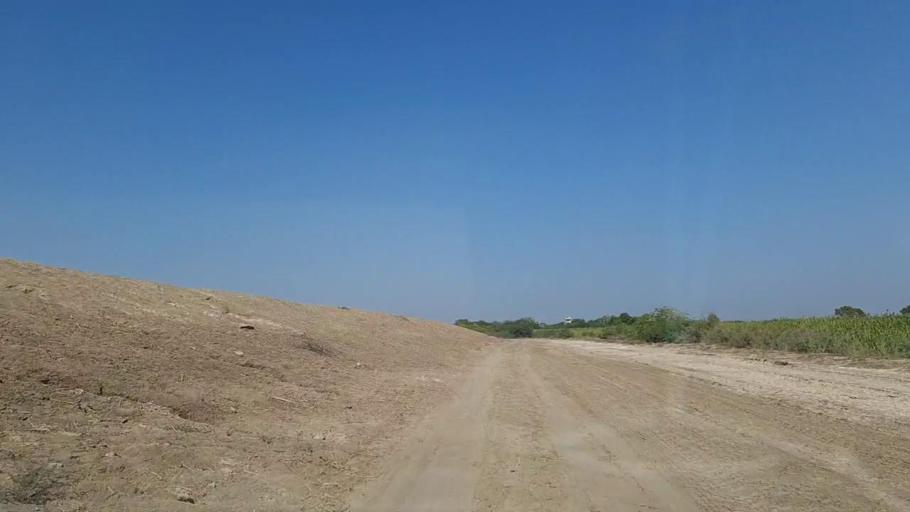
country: PK
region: Sindh
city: Chuhar Jamali
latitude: 24.4871
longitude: 68.0159
